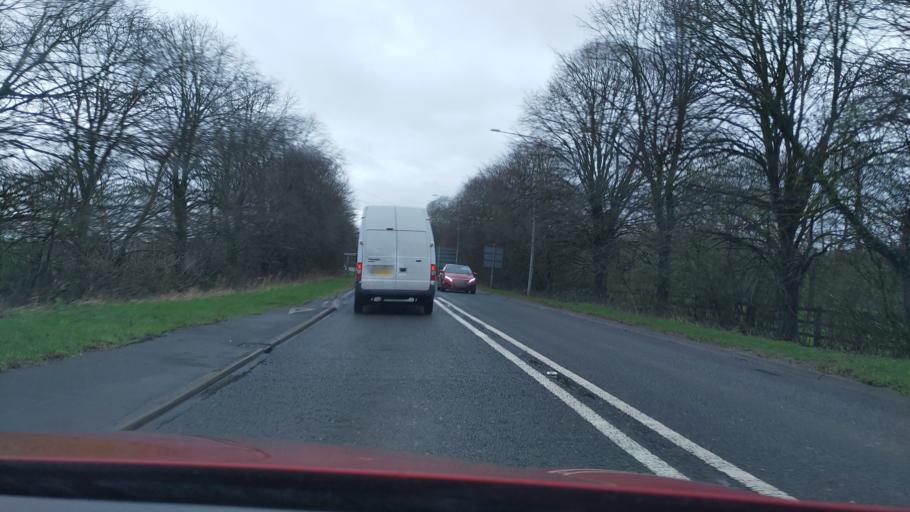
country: GB
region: England
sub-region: Lancashire
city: Leyland
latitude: 53.7199
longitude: -2.6855
